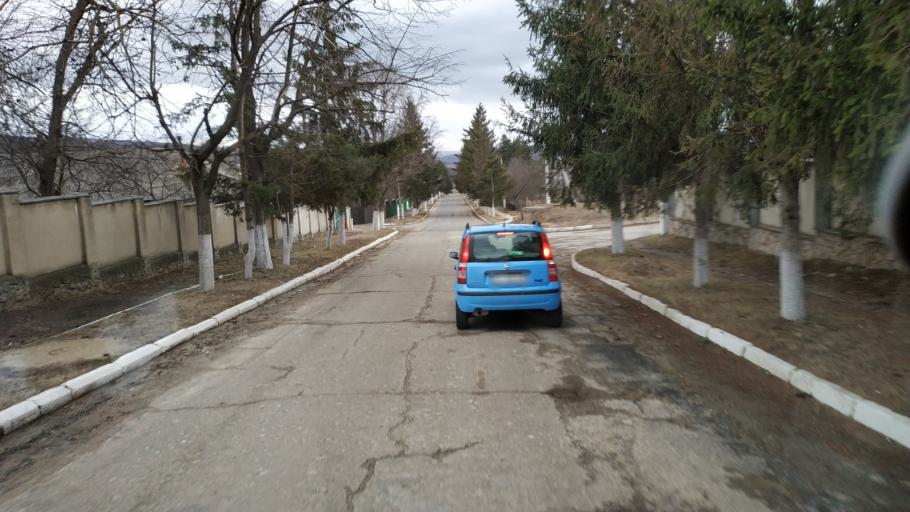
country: MD
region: Calarasi
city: Calarasi
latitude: 47.2062
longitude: 28.2431
